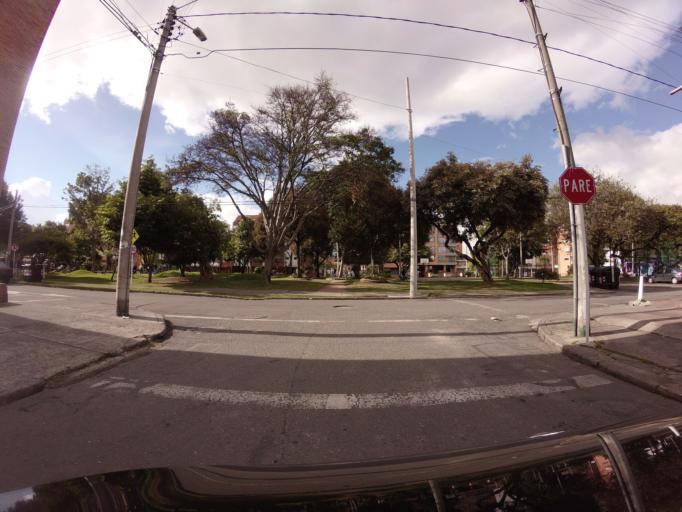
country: CO
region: Bogota D.C.
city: Barrio San Luis
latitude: 4.7045
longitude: -74.0575
